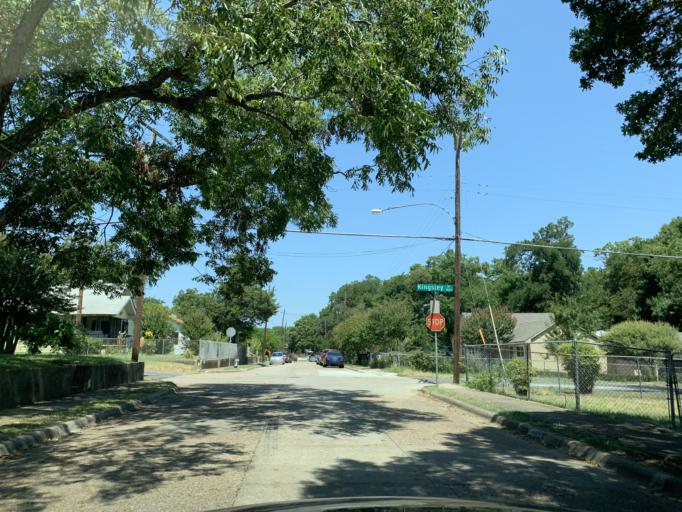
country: US
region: Texas
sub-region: Dallas County
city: Hutchins
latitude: 32.6873
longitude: -96.7957
